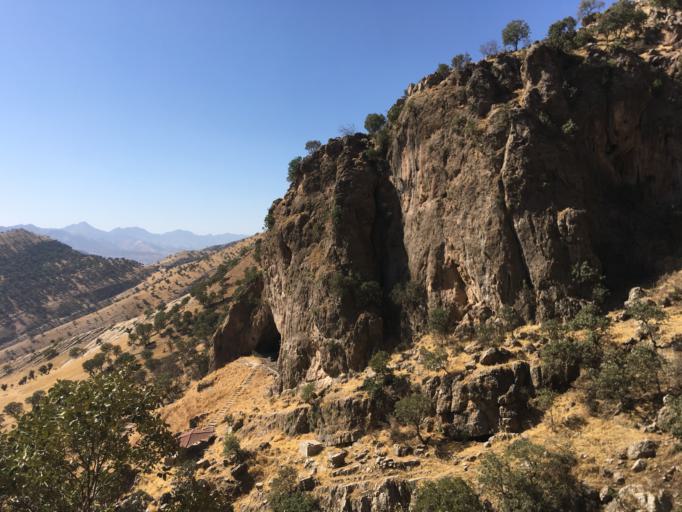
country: IQ
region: Arbil
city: Mergasur
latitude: 36.8346
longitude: 44.2207
